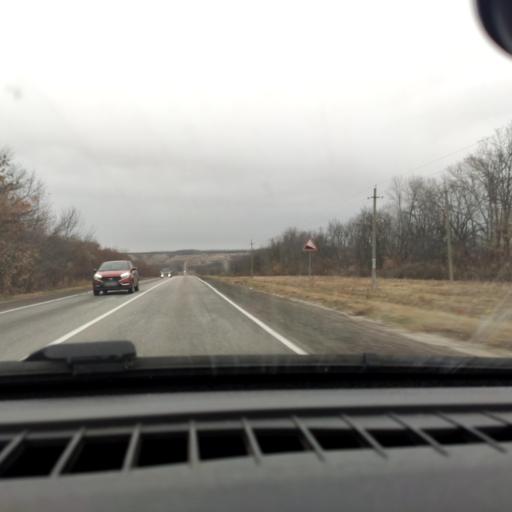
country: RU
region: Voronezj
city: Uryv-Pokrovka
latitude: 51.1137
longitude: 39.0281
